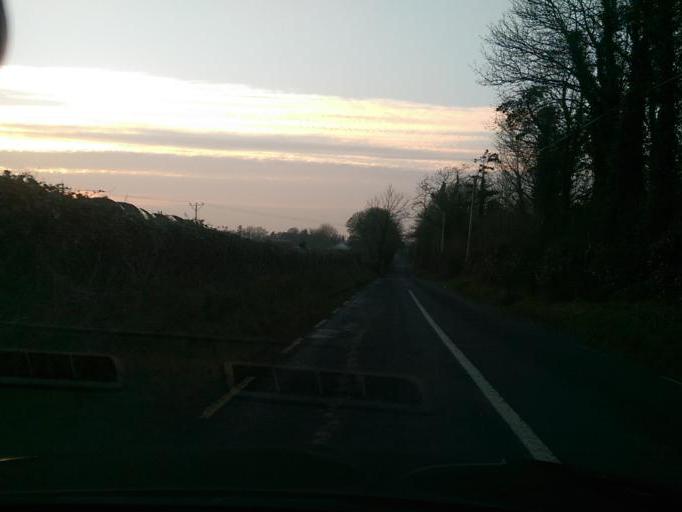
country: IE
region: Connaught
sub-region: County Galway
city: Loughrea
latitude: 53.2332
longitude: -8.6493
